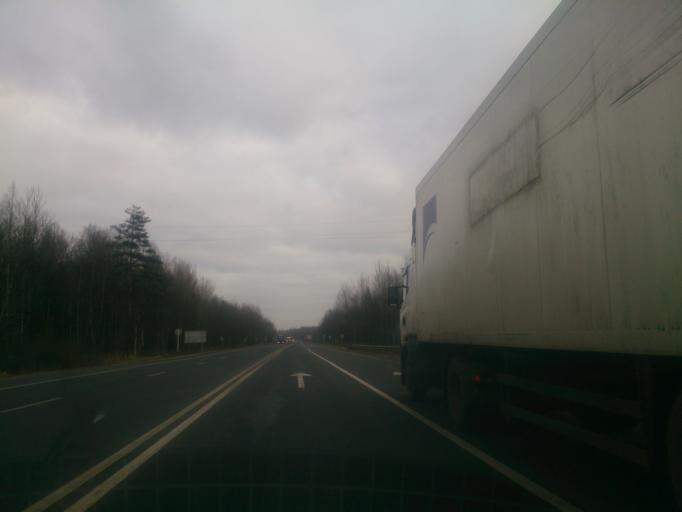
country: RU
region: Novgorod
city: Chudovo
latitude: 59.0026
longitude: 31.5564
